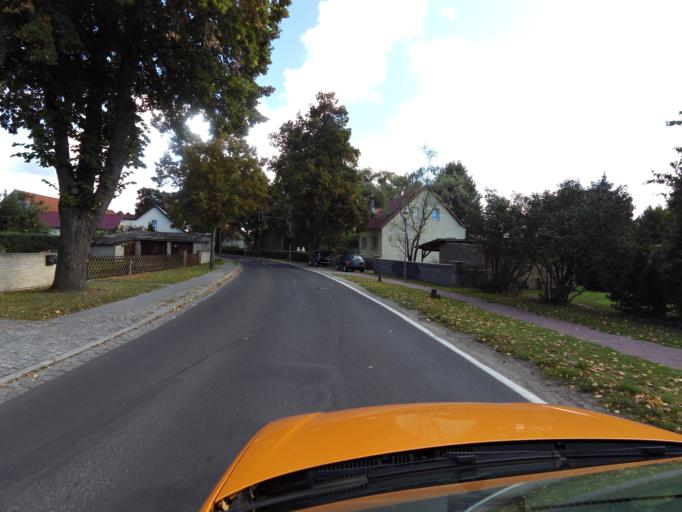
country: DE
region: Brandenburg
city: Michendorf
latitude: 52.2845
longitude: 13.0630
